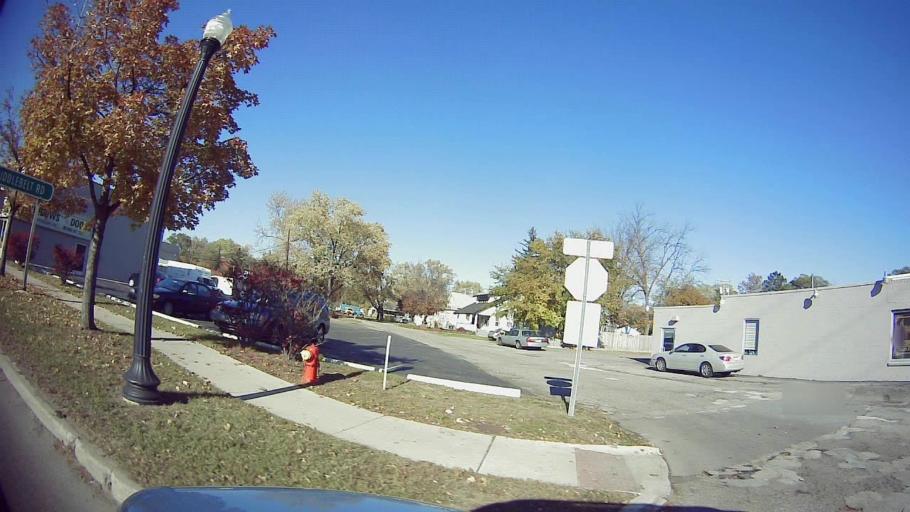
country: US
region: Michigan
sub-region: Oakland County
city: Farmington
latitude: 42.4477
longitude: -83.3348
